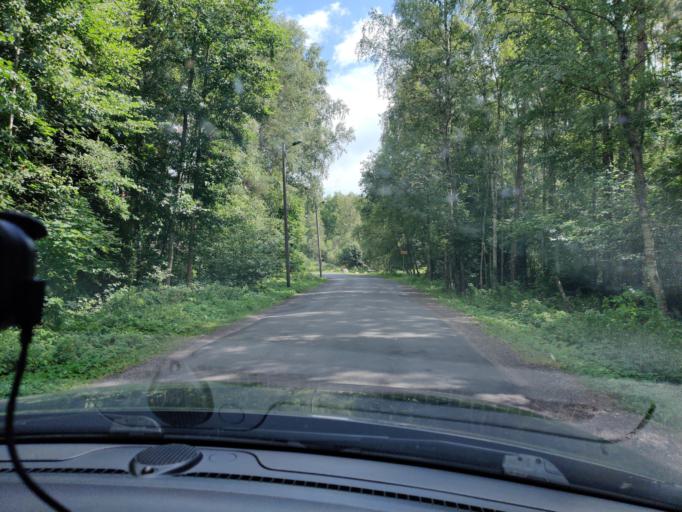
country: EE
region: Harju
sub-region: Saue vald
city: Laagri
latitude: 59.3894
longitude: 24.6449
